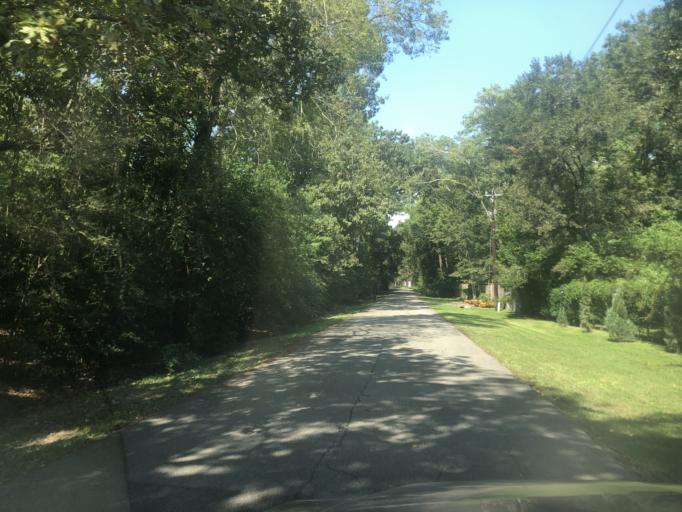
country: US
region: Texas
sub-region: Harris County
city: Bunker Hill Village
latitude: 29.7499
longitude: -95.5429
